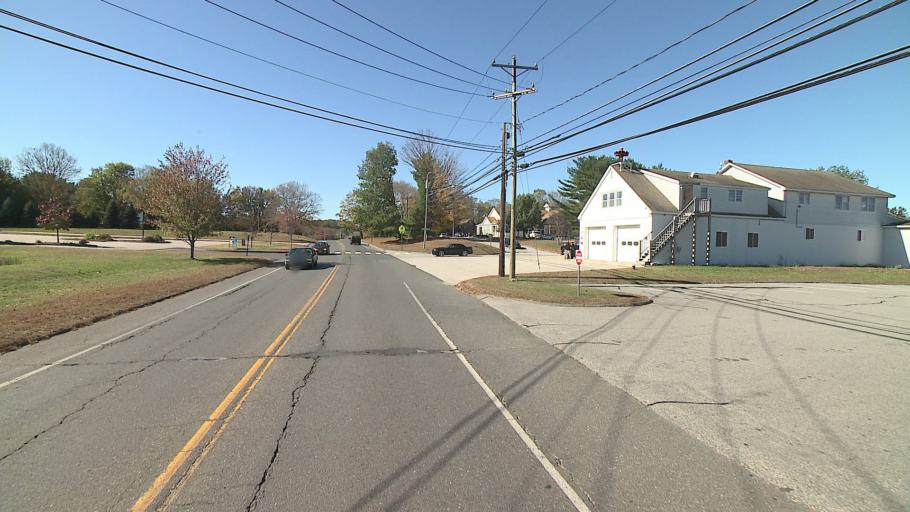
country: US
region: Connecticut
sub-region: Tolland County
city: South Coventry
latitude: 41.7034
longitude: -72.2993
